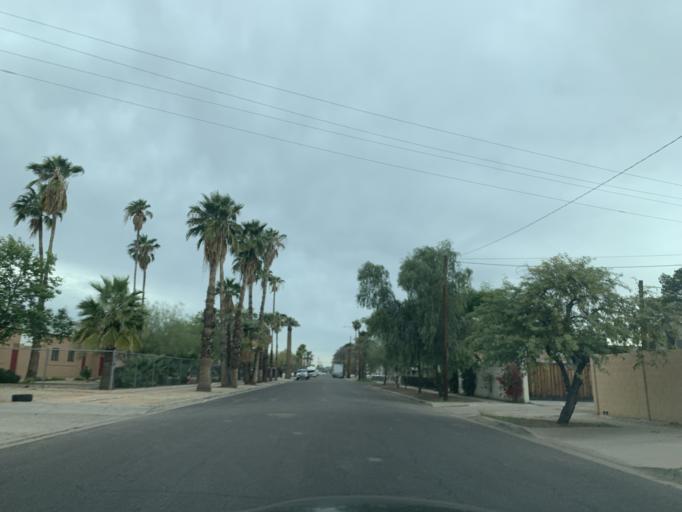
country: US
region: Arizona
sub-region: Maricopa County
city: Phoenix
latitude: 33.4630
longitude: -112.0499
